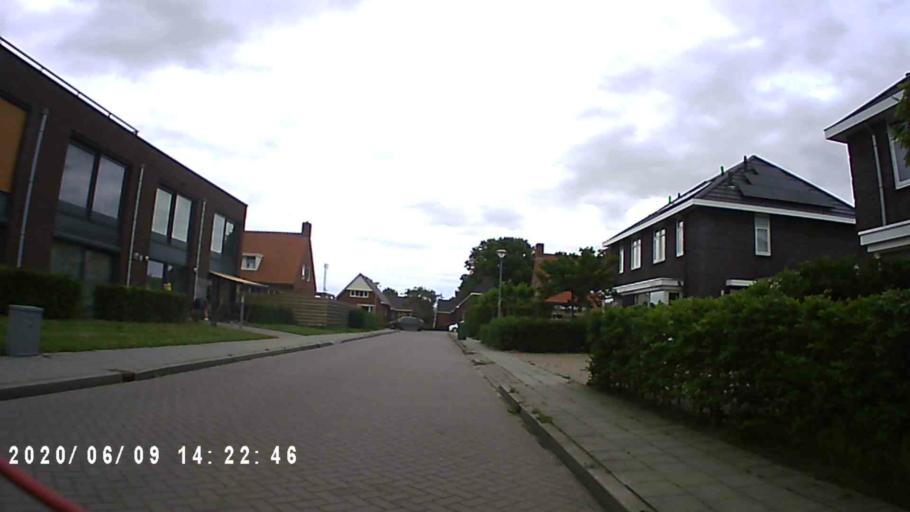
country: NL
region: Groningen
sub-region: Gemeente Bedum
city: Bedum
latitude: 53.3011
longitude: 6.5907
